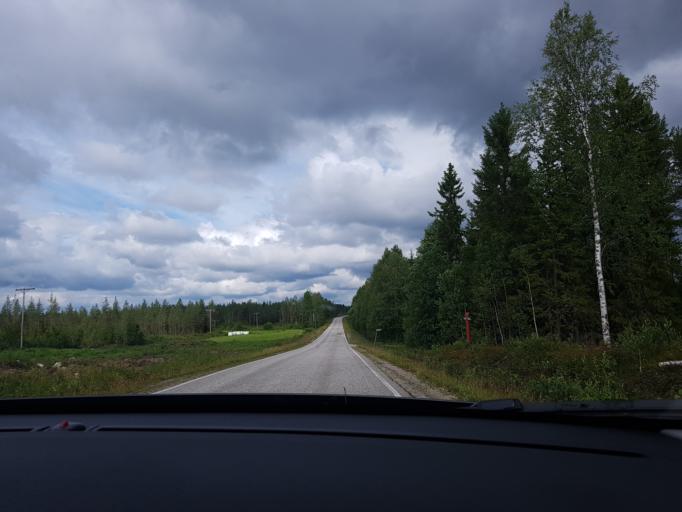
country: FI
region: Kainuu
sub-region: Kehys-Kainuu
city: Kuhmo
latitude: 64.2690
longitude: 29.3794
